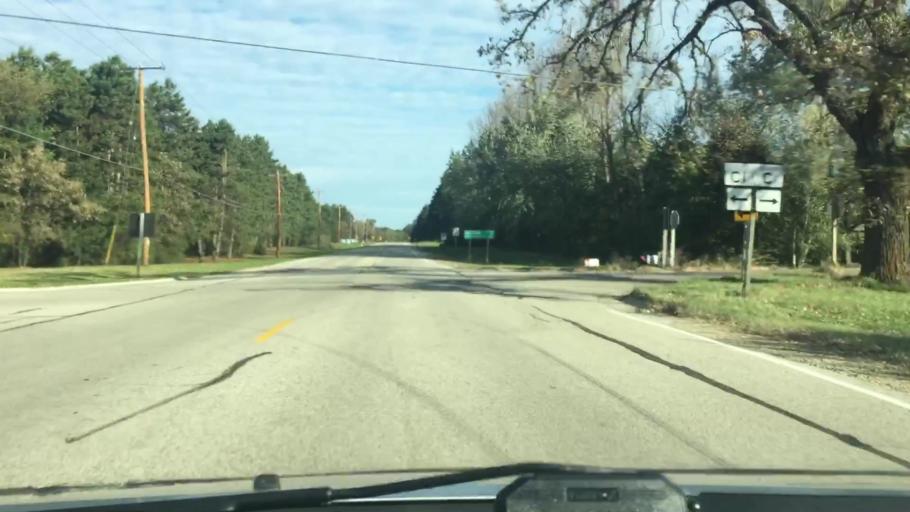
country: US
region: Wisconsin
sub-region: Waukesha County
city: Dousman
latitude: 42.9529
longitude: -88.4785
